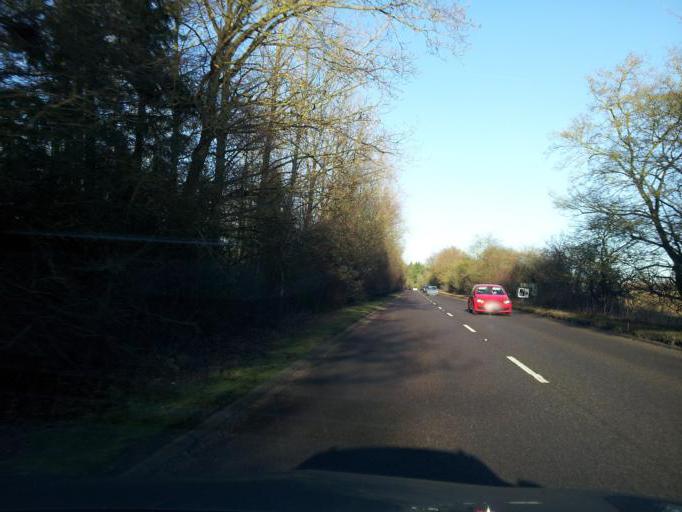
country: GB
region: England
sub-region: Suffolk
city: Lavenham
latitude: 52.1314
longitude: 0.7526
